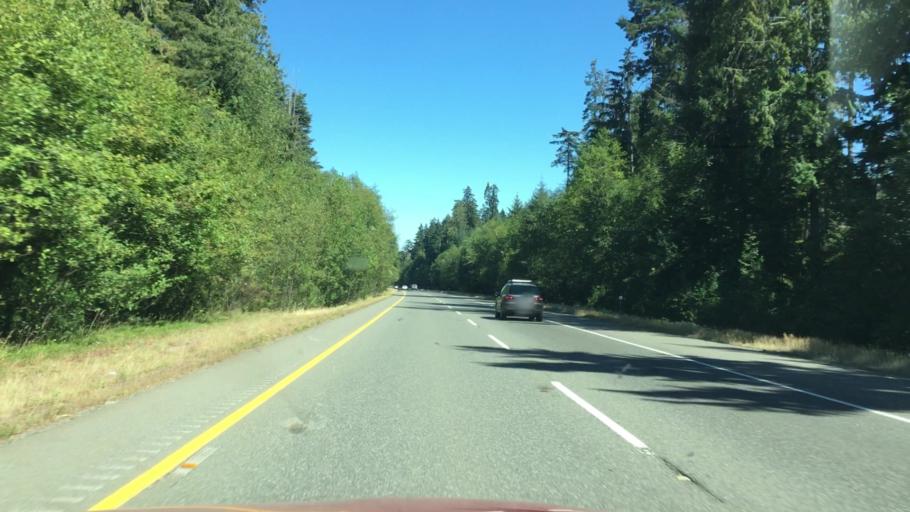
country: CA
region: British Columbia
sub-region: Regional District of Nanaimo
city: Parksville
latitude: 49.3177
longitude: -124.3904
